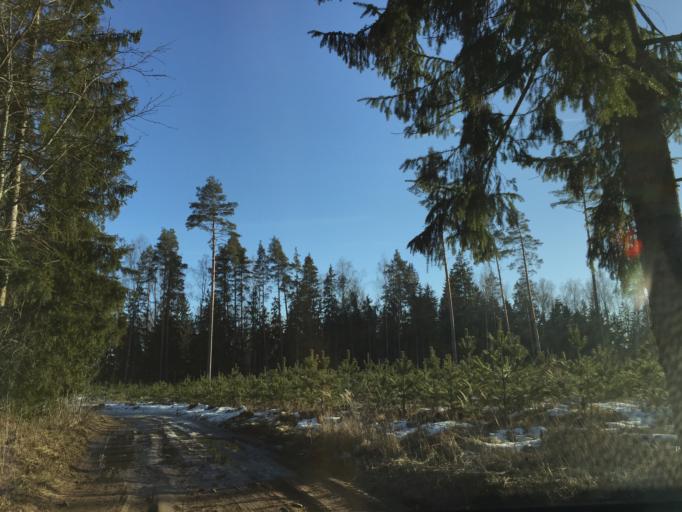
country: LV
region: Lecava
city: Iecava
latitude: 56.6910
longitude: 24.0768
